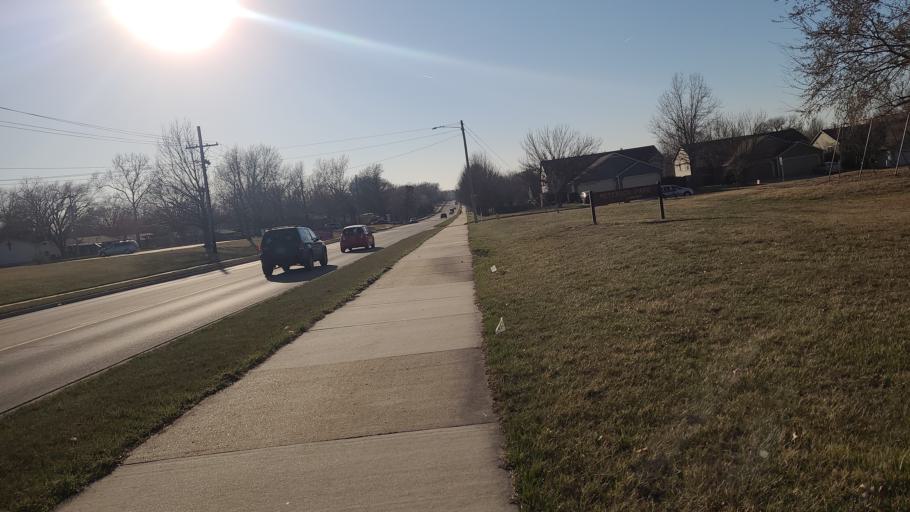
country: US
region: Kansas
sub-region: Douglas County
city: Lawrence
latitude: 38.9862
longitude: -95.2617
